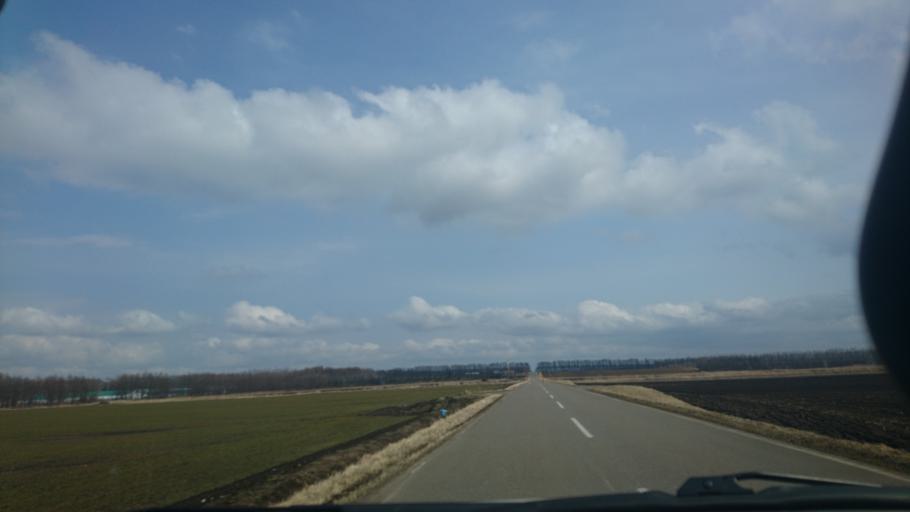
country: JP
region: Hokkaido
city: Otofuke
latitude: 43.2058
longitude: 143.2833
